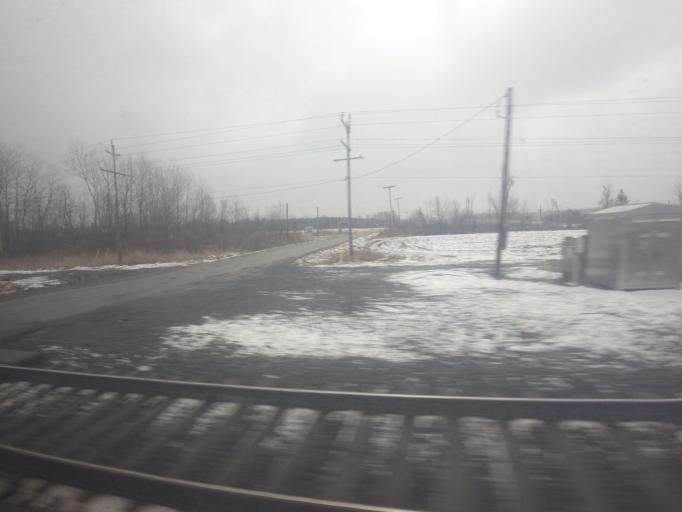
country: CA
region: Ontario
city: Quinte West
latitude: 44.0296
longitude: -77.7639
